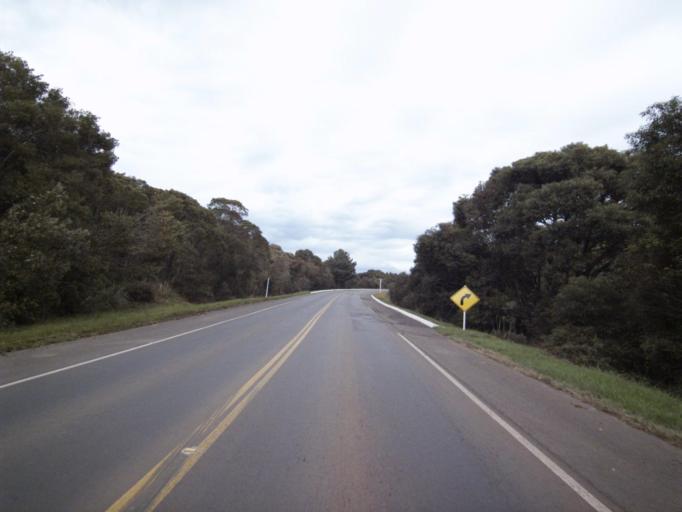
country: BR
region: Santa Catarina
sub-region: Concordia
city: Concordia
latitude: -26.9680
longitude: -51.8510
